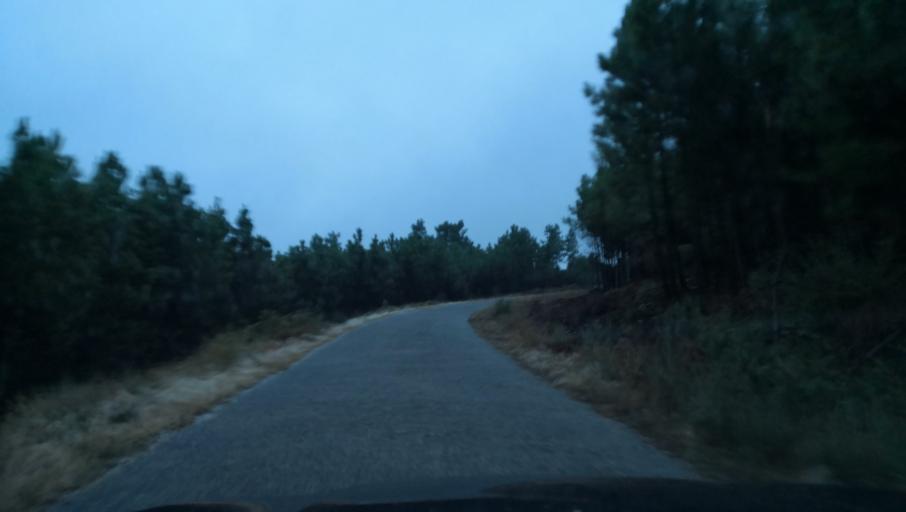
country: PT
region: Vila Real
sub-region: Sabrosa
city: Sabrosa
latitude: 41.2844
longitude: -7.5790
